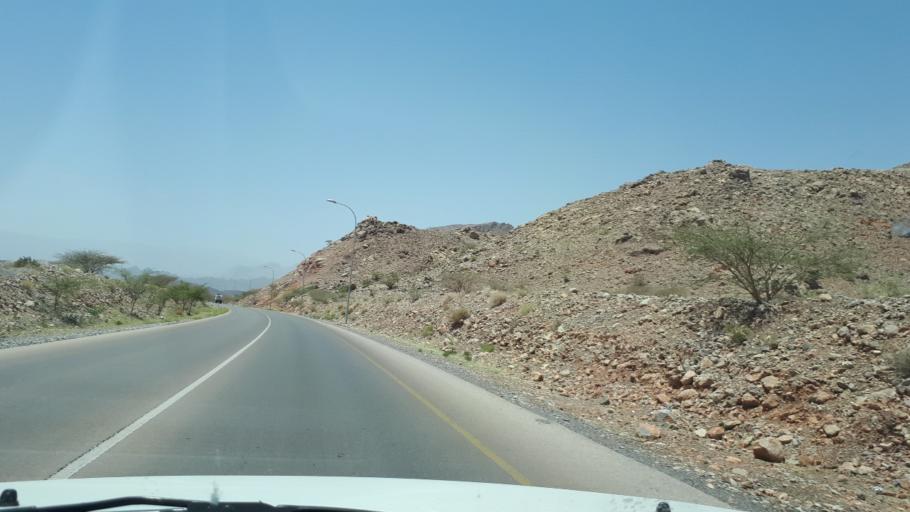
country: OM
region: Muhafazat ad Dakhiliyah
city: Bahla'
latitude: 23.0515
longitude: 57.3072
